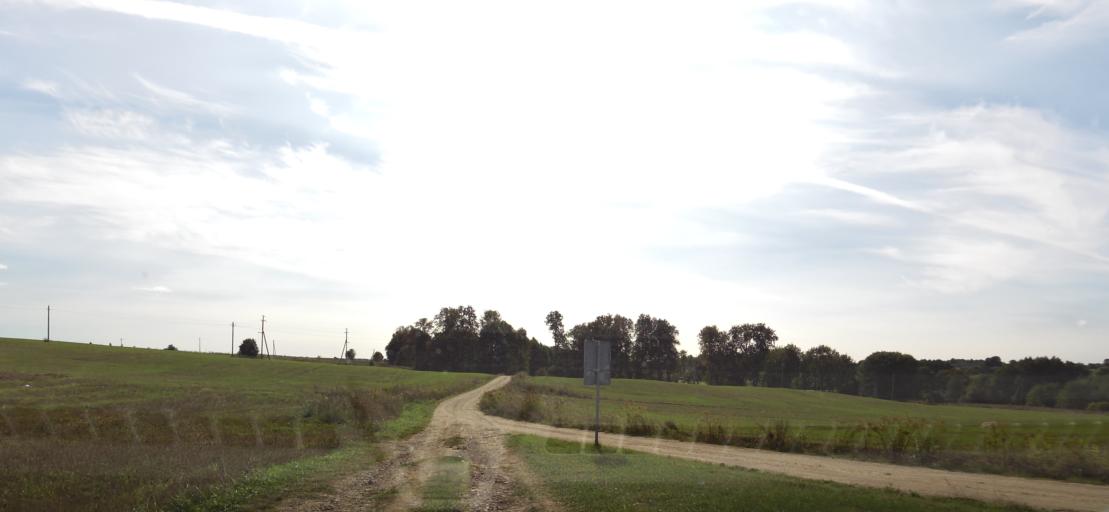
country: LT
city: Skaidiskes
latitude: 54.4596
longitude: 25.4784
